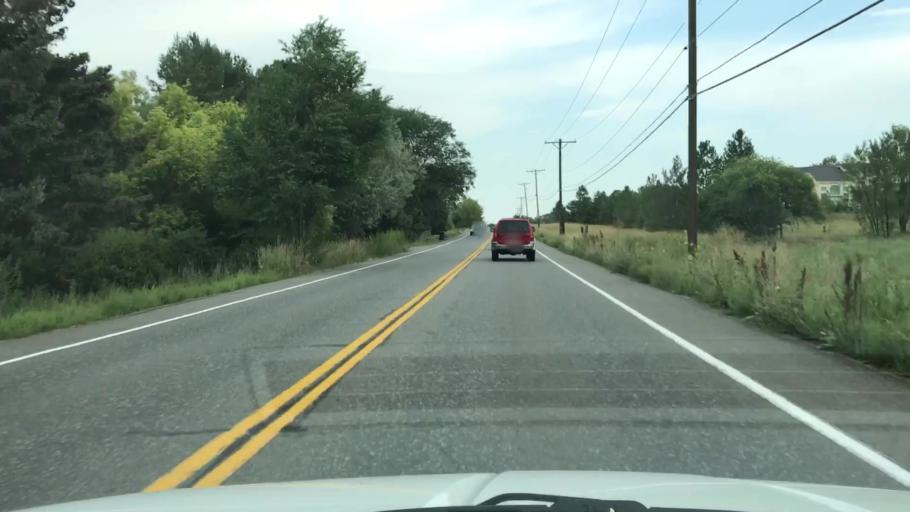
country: US
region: Colorado
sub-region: Boulder County
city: Louisville
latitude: 40.0001
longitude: -105.1474
